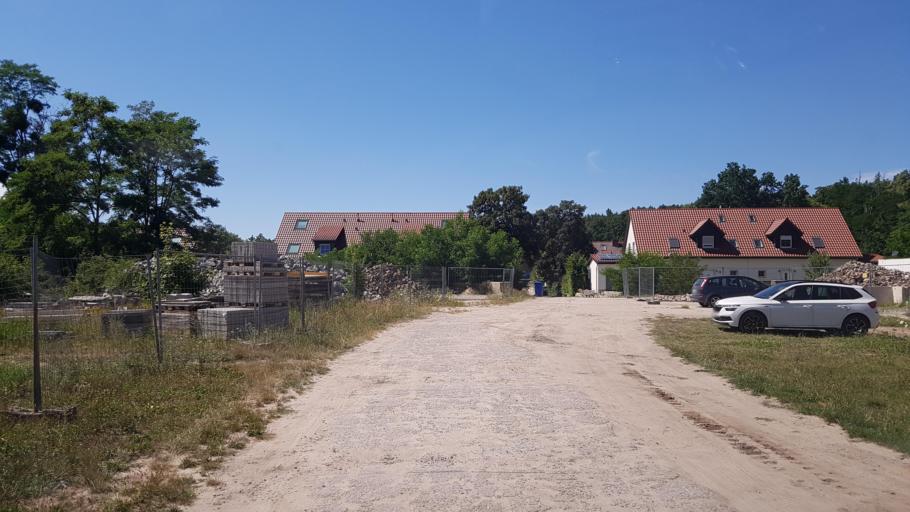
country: DE
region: Brandenburg
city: Trebbin
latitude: 52.2420
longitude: 13.1490
